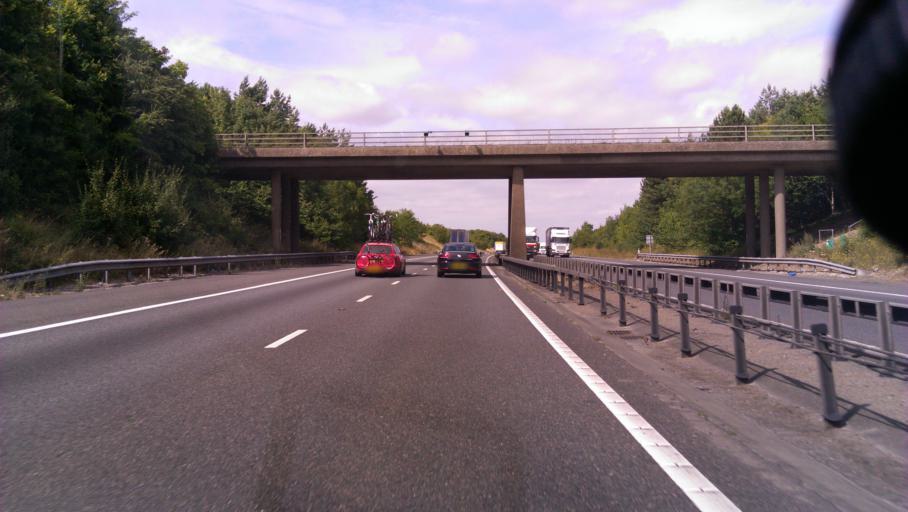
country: GB
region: England
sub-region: Essex
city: Saffron Walden
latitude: 52.0352
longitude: 0.1895
